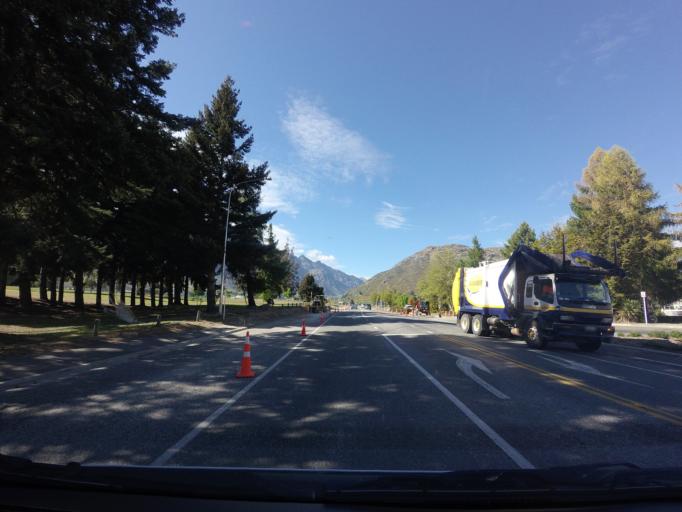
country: NZ
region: Otago
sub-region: Queenstown-Lakes District
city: Queenstown
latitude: -45.0171
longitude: 168.7322
